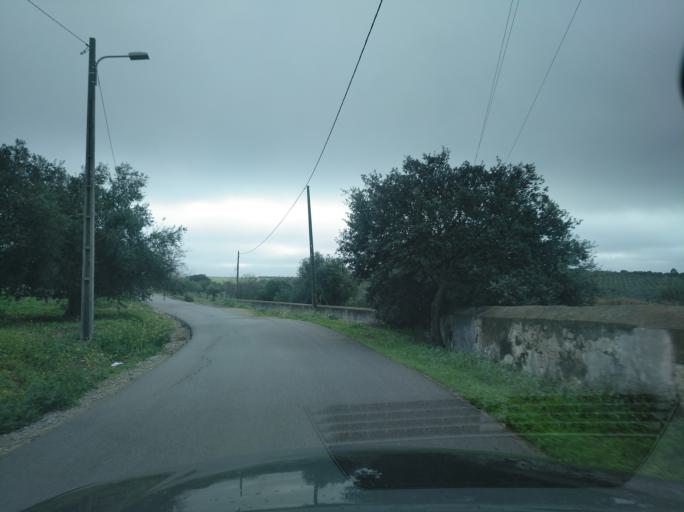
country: PT
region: Portalegre
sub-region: Elvas
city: Elvas
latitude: 38.8647
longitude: -7.1658
